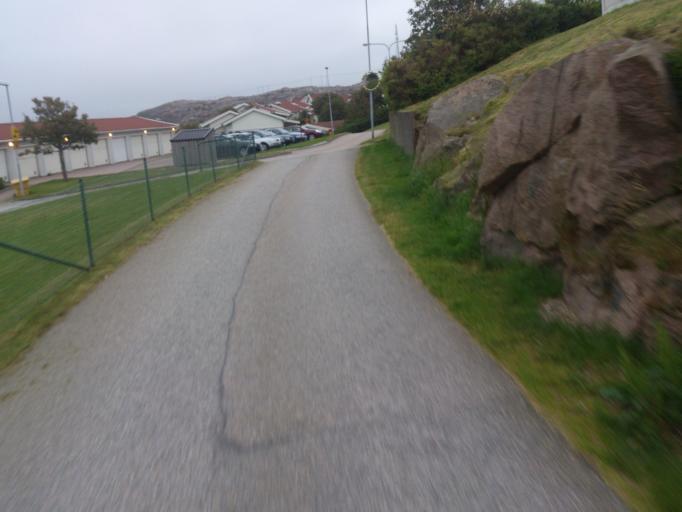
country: SE
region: Vaestra Goetaland
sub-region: Sotenas Kommun
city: Kungshamn
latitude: 58.3779
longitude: 11.2607
